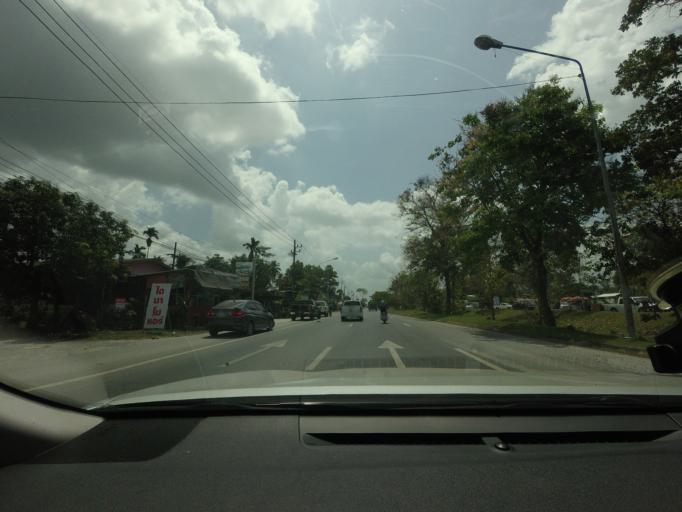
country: TH
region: Nakhon Si Thammarat
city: Nakhon Si Thammarat
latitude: 8.4260
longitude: 99.9216
